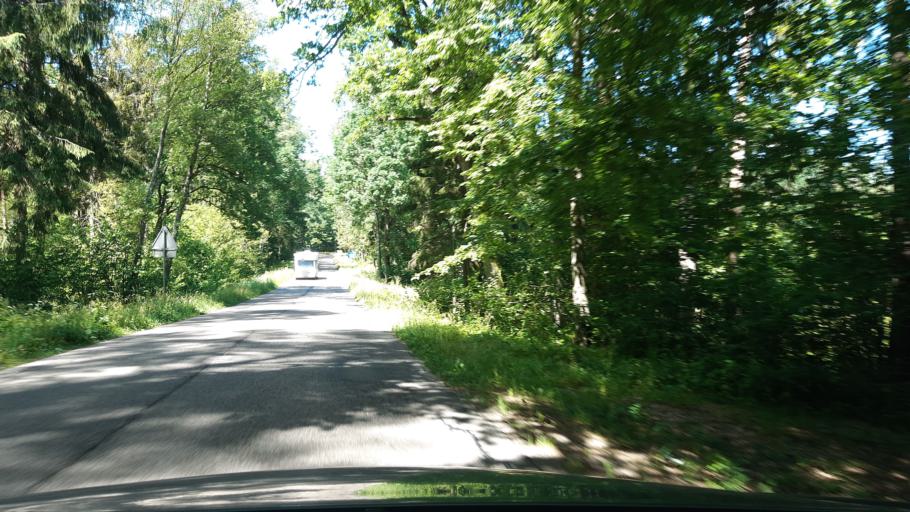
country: PL
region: Warmian-Masurian Voivodeship
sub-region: Powiat mragowski
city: Mikolajki
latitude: 53.7526
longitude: 21.5001
